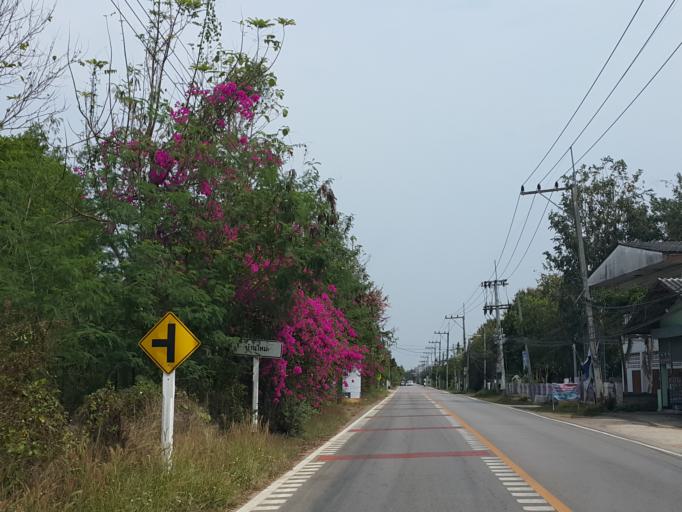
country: TH
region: Lampang
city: Ko Kha
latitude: 18.1725
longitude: 99.3894
